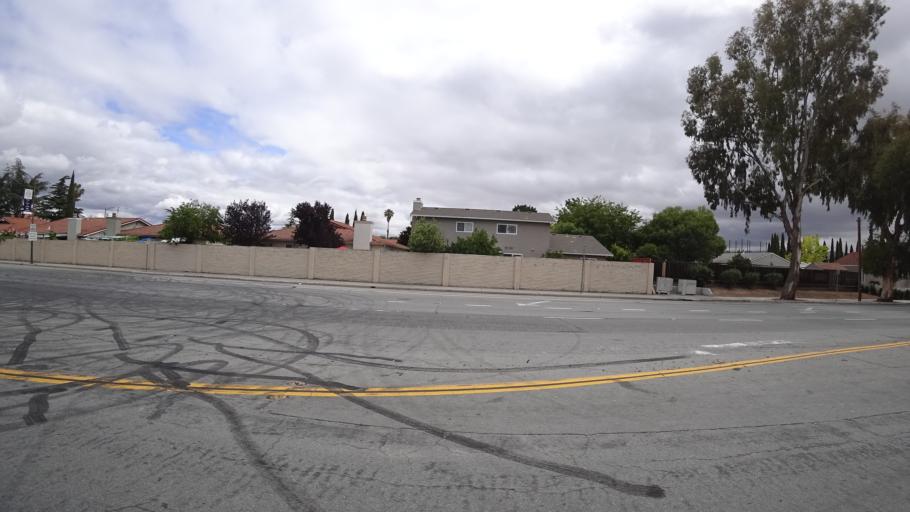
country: US
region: California
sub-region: Santa Clara County
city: Seven Trees
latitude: 37.2983
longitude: -121.8383
